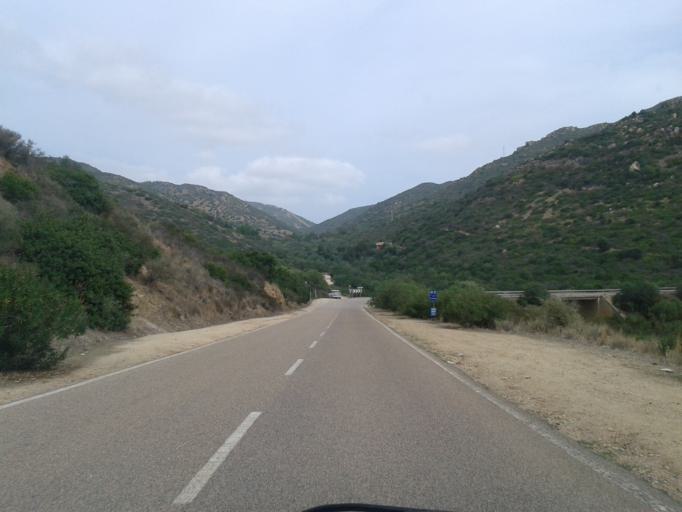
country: IT
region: Sardinia
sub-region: Provincia di Cagliari
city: Villasimius
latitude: 39.1441
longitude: 9.5474
